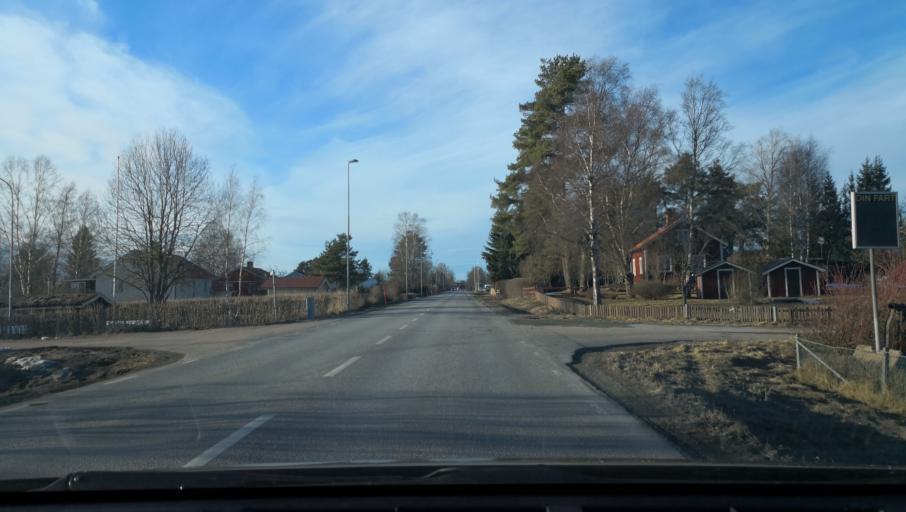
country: SE
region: Uppsala
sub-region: Osthammars Kommun
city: OEsthammar
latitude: 60.2820
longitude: 18.2950
